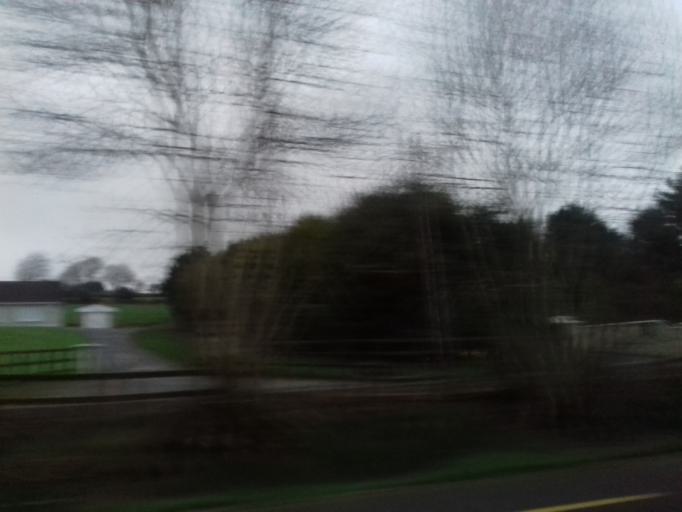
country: IE
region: Munster
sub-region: Ciarrai
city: Castleisland
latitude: 52.2941
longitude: -9.3936
